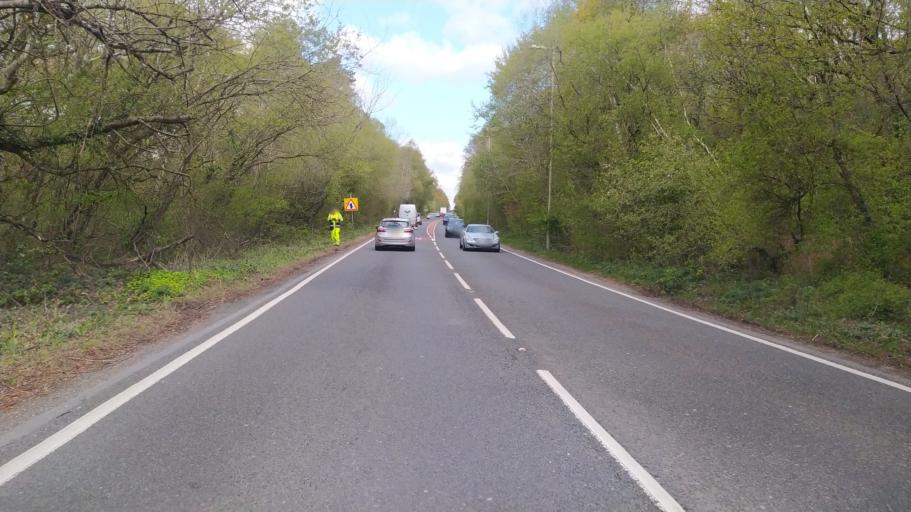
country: GB
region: England
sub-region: Hampshire
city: Marchwood
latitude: 50.8884
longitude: -1.4642
